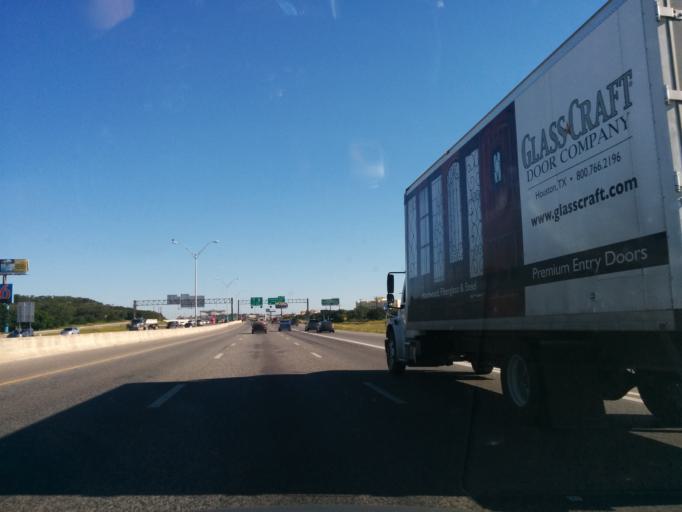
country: US
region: Texas
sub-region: Bexar County
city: Shavano Park
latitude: 29.5949
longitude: -98.5989
